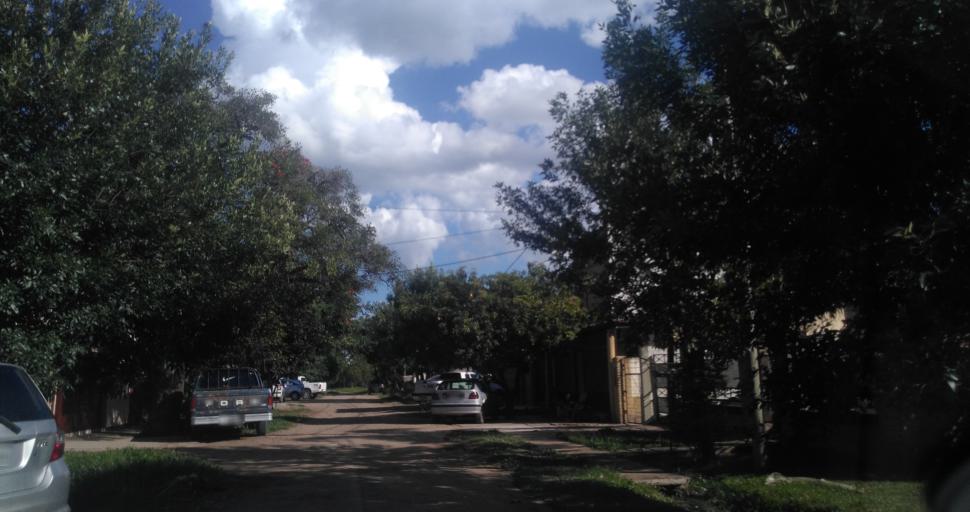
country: AR
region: Chaco
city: Resistencia
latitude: -27.4378
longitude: -58.9623
